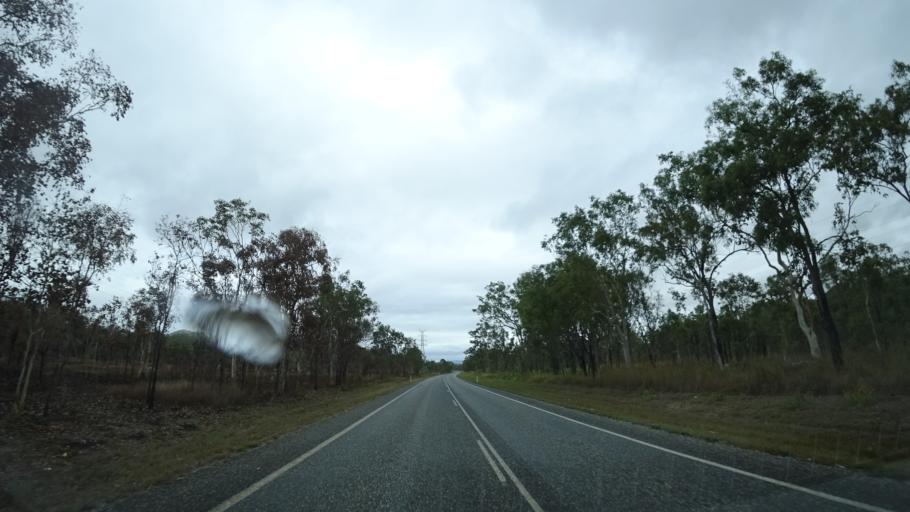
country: AU
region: Queensland
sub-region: Tablelands
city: Mareeba
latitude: -16.7376
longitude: 145.3498
